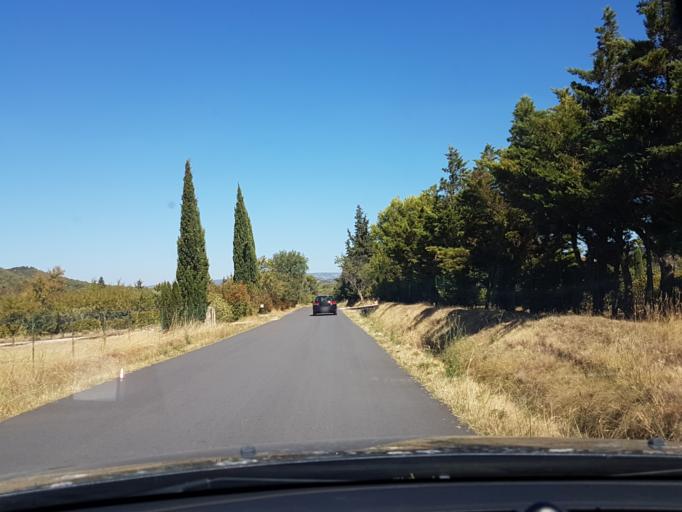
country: FR
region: Provence-Alpes-Cote d'Azur
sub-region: Departement des Bouches-du-Rhone
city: Eygalieres
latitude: 43.7613
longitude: 4.9583
